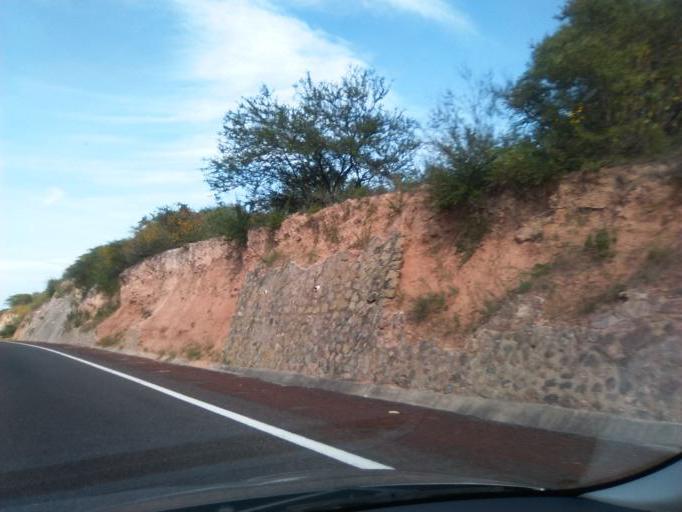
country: MX
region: Guerrero
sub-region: Huitzuco de los Figueroa
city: San Francisco Ozomatlan
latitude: 18.0551
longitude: -99.2496
